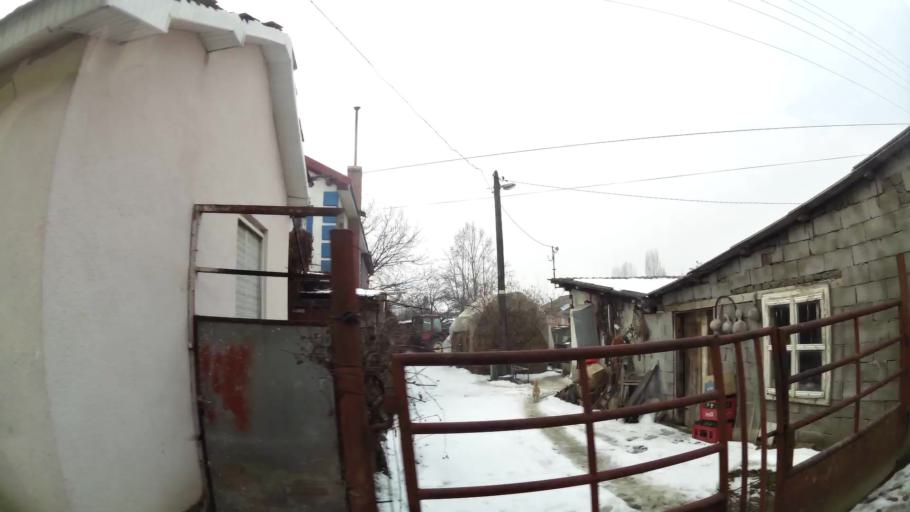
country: MK
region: Ilinden
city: Jurumleri
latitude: 41.9739
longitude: 21.5413
